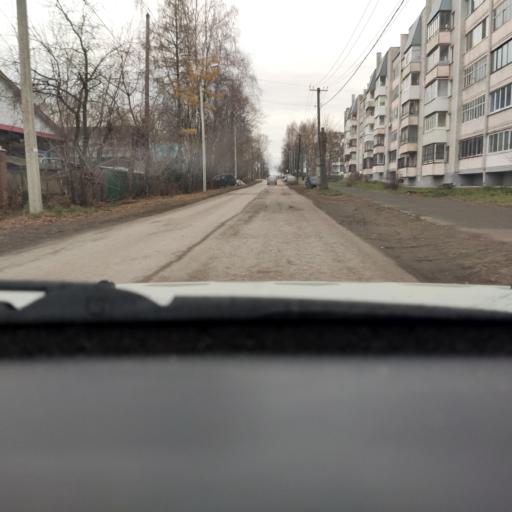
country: RU
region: Perm
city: Polazna
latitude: 58.1295
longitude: 56.3901
